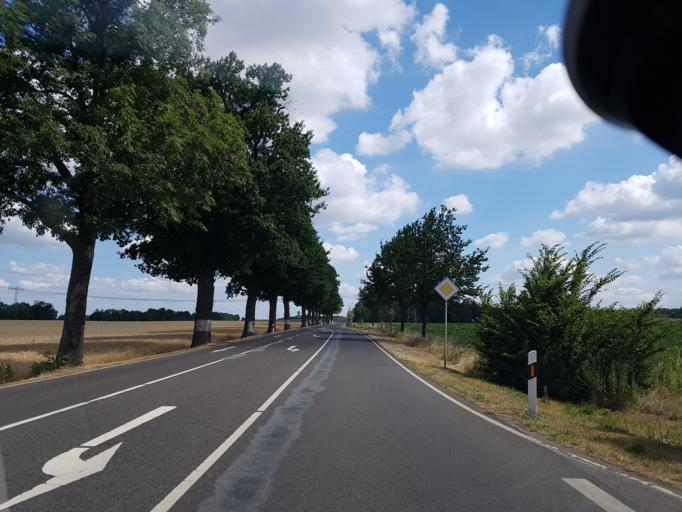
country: DE
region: Brandenburg
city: Drebkau
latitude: 51.6591
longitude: 14.2354
